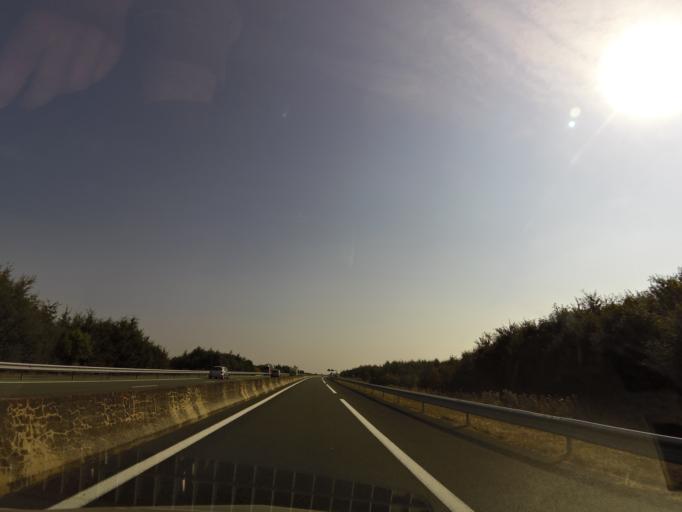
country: FR
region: Pays de la Loire
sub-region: Departement de la Vendee
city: Les Essarts
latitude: 46.8065
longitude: -1.2117
